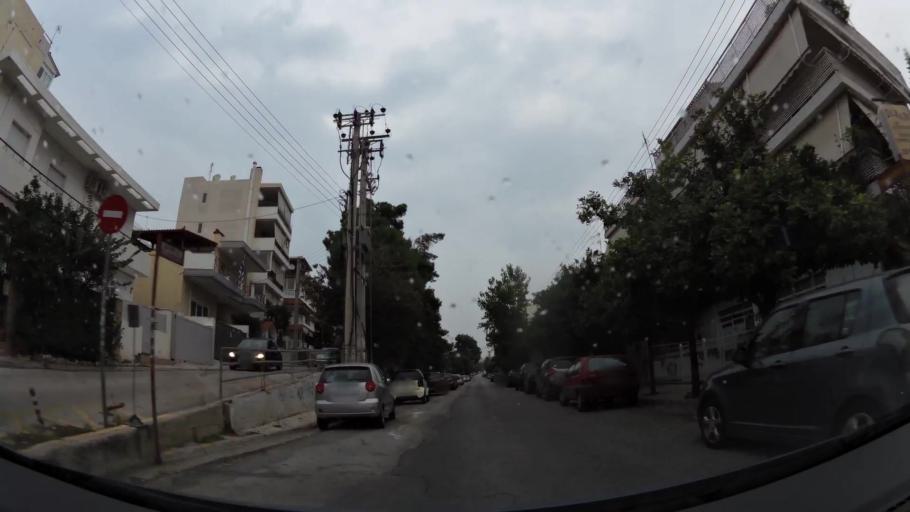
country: GR
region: Attica
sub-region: Nomarchia Athinas
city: Argyroupoli
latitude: 37.9072
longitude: 23.7415
